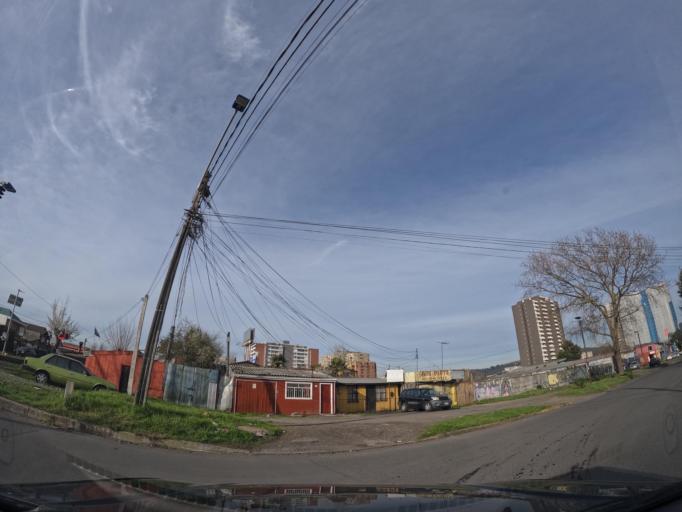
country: CL
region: Biobio
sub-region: Provincia de Concepcion
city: Concepcion
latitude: -36.8126
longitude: -73.0505
